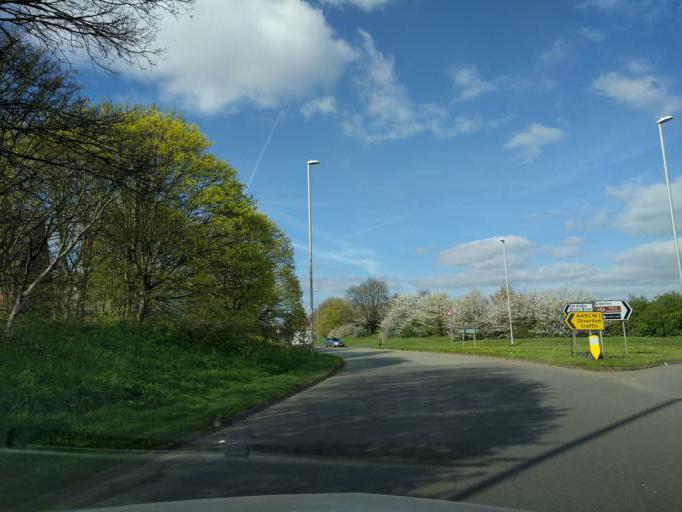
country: GB
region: England
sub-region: Northamptonshire
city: Earls Barton
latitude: 52.2516
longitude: -0.8090
